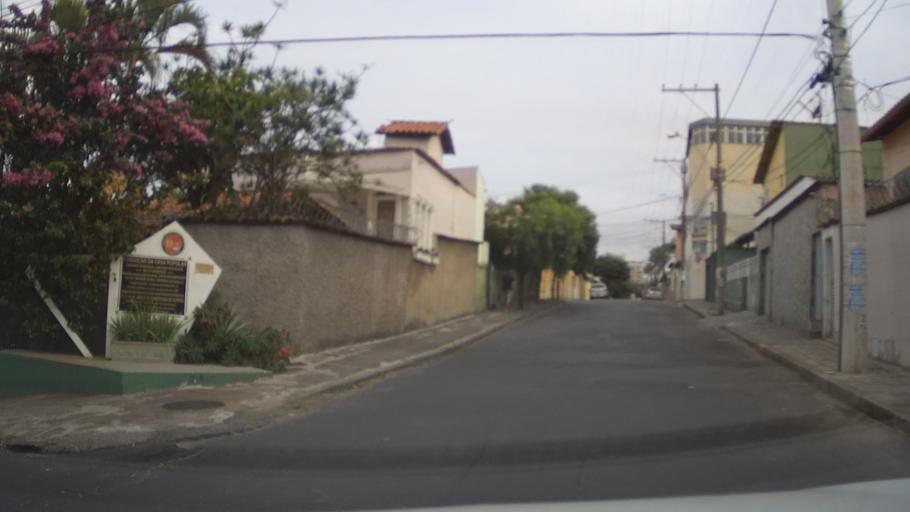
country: BR
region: Minas Gerais
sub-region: Belo Horizonte
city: Belo Horizonte
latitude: -19.9118
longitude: -43.9732
